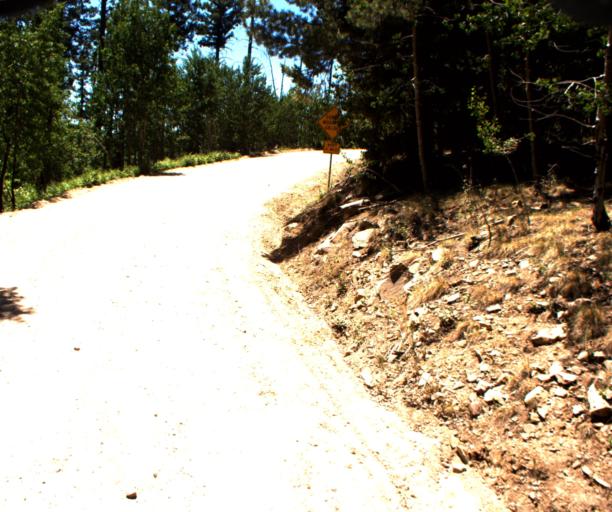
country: US
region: Arizona
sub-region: Graham County
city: Swift Trail Junction
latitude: 32.6939
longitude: -109.9068
